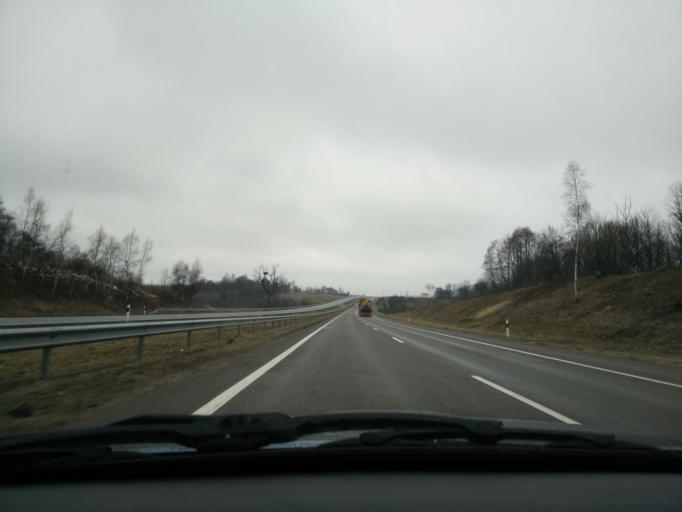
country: LT
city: Silale
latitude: 55.5165
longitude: 22.3782
